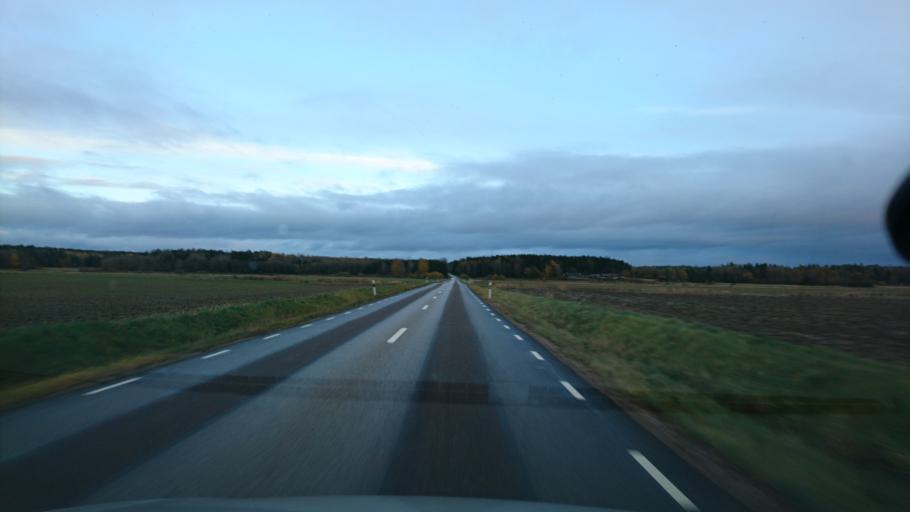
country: SE
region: Uppsala
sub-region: Uppsala Kommun
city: Vattholma
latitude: 59.9498
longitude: 17.9202
